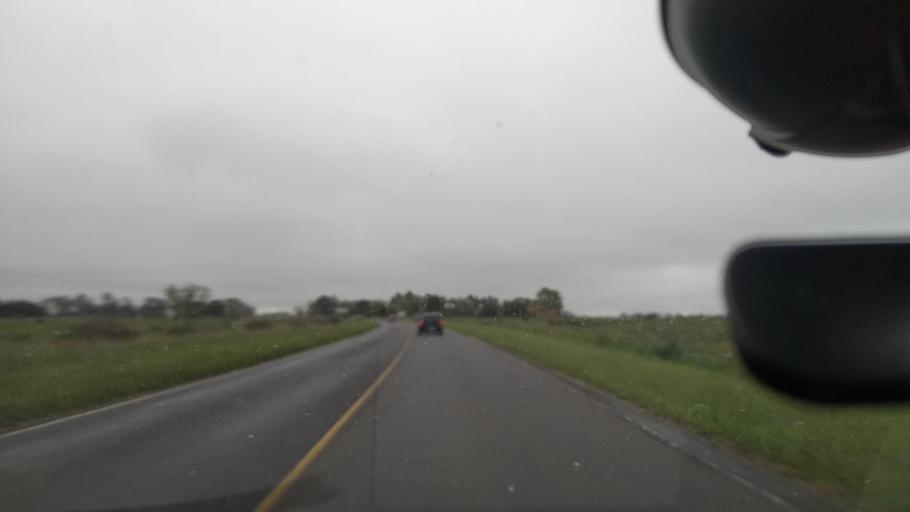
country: AR
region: Buenos Aires
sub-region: Partido de Magdalena
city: Magdalena
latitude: -35.2290
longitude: -57.7125
